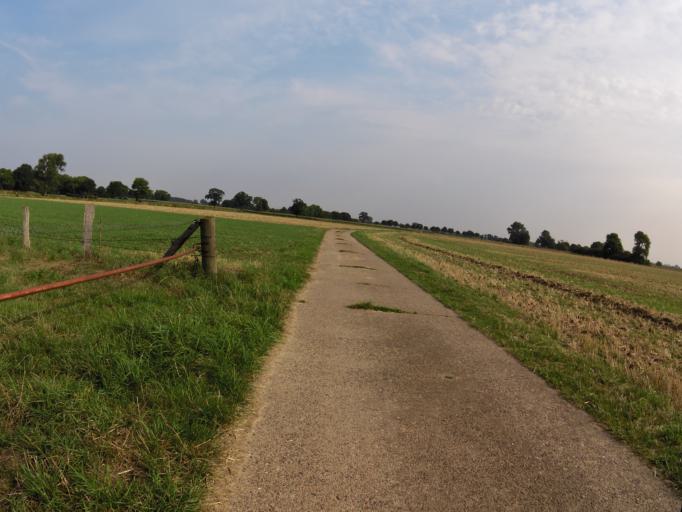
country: DE
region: Lower Saxony
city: Raddestorf
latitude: 52.4718
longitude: 9.0151
